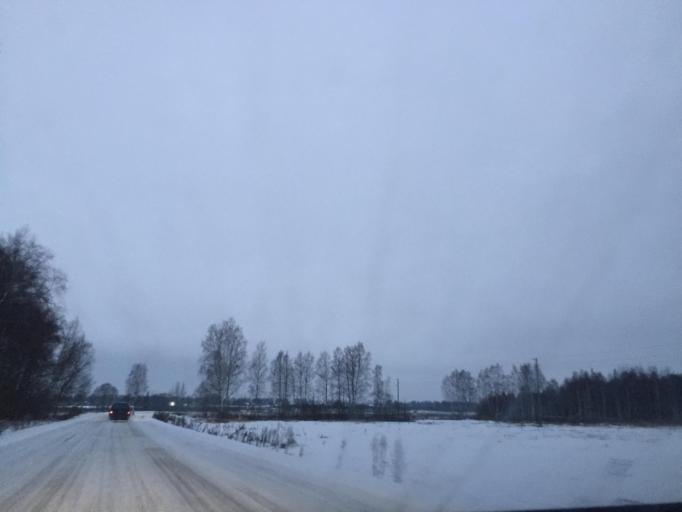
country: LV
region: Raunas
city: Rauna
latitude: 57.4259
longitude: 25.6419
